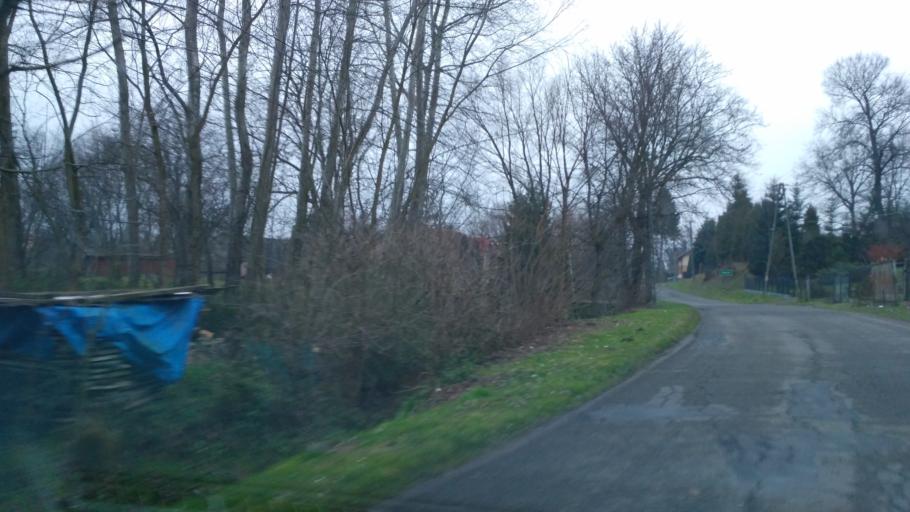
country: PL
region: Subcarpathian Voivodeship
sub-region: Powiat przeworski
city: Mirocin
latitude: 50.0445
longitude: 22.5546
